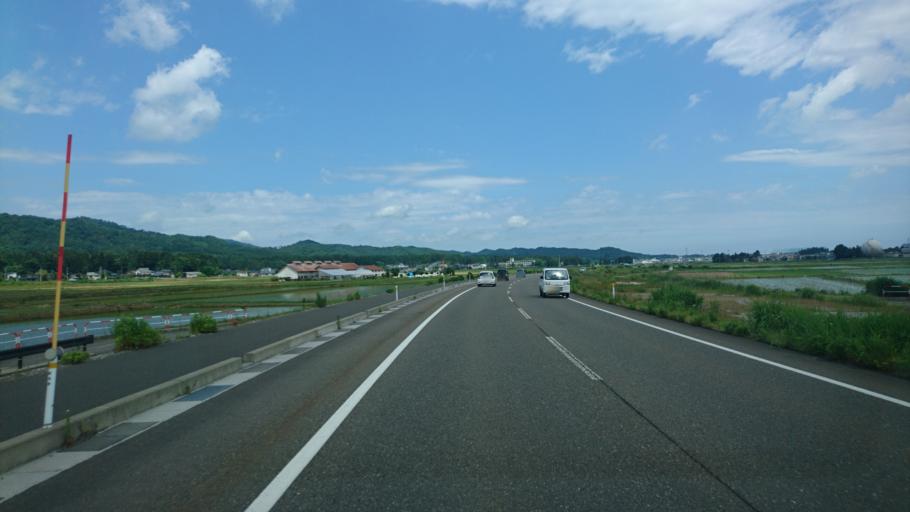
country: JP
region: Niigata
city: Arai
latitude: 37.0734
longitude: 138.2357
